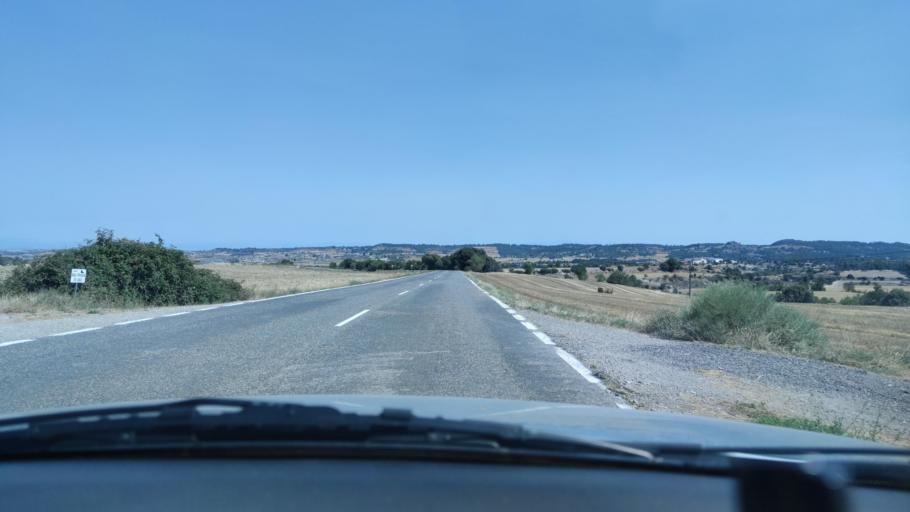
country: ES
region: Catalonia
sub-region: Provincia de Lleida
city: Sant Guim de Freixenet
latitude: 41.6137
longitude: 1.3431
